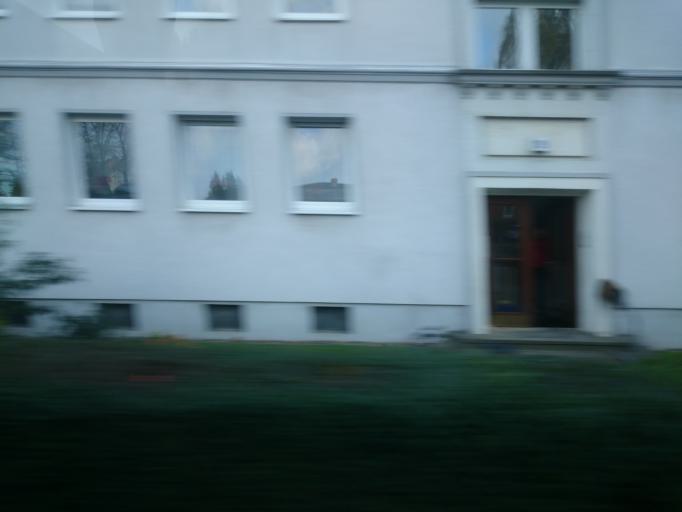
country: DE
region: Mecklenburg-Vorpommern
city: Warnemuende
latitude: 54.1728
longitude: 12.0859
